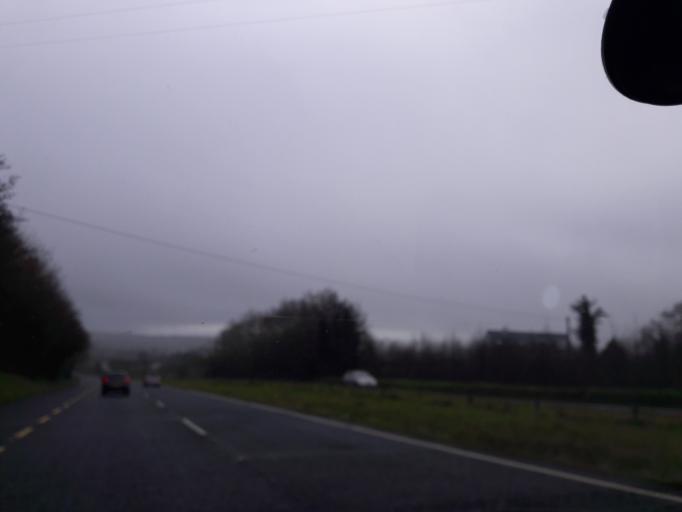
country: IE
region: Ulster
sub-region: County Donegal
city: Letterkenny
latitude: 54.9487
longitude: -7.6513
